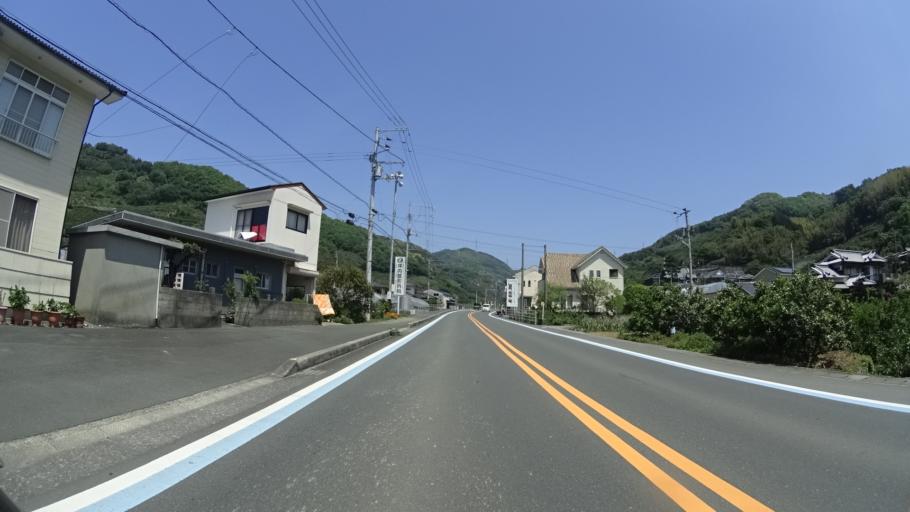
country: JP
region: Ehime
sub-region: Nishiuwa-gun
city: Ikata-cho
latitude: 33.4941
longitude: 132.3971
